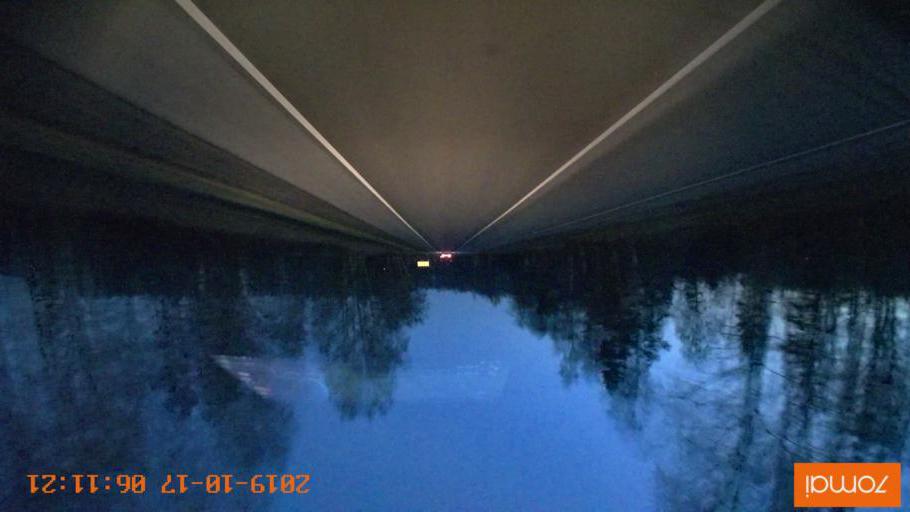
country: RU
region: Ivanovo
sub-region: Gorod Ivanovo
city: Ivanovo
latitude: 56.9204
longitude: 40.9583
